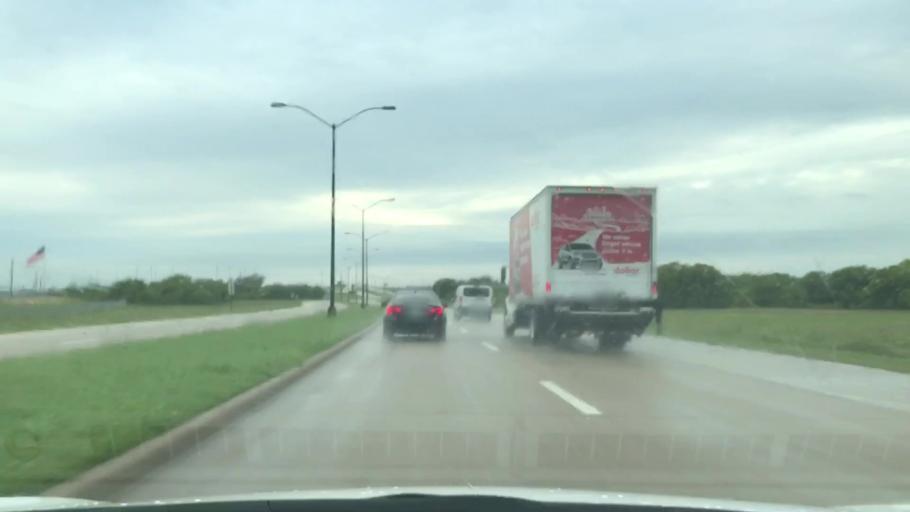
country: US
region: Texas
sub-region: Dallas County
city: Coppell
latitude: 32.9255
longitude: -97.0307
